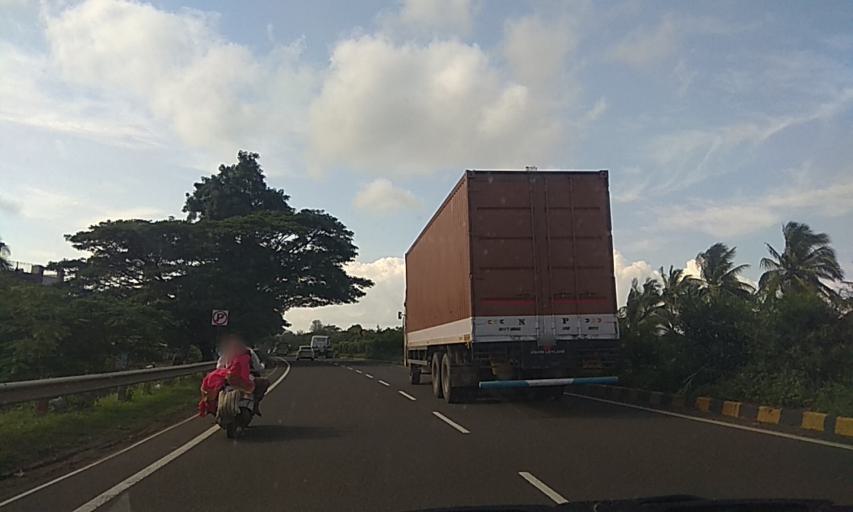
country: IN
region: Maharashtra
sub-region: Kolhapur
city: Kodoli
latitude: 16.9268
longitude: 74.2886
